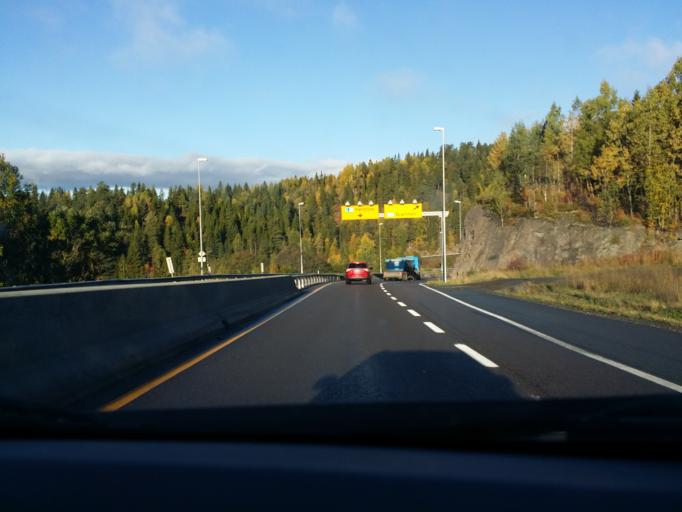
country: NO
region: Buskerud
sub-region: Hole
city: Vik
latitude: 59.9770
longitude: 10.3254
